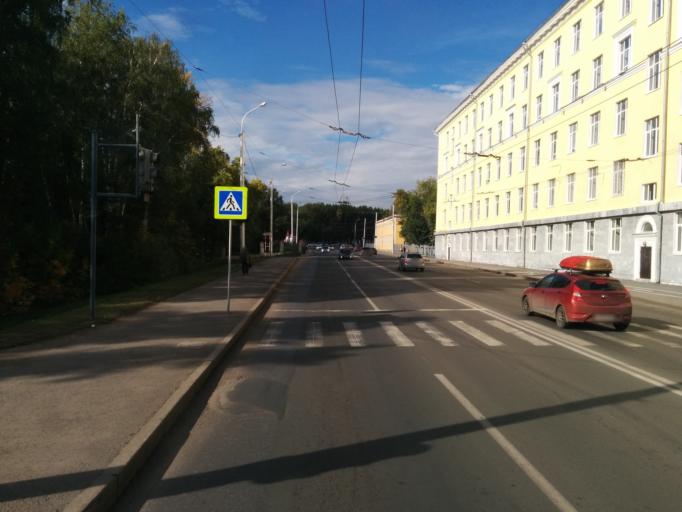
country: RU
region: Bashkortostan
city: Ufa
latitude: 54.8179
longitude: 56.0574
